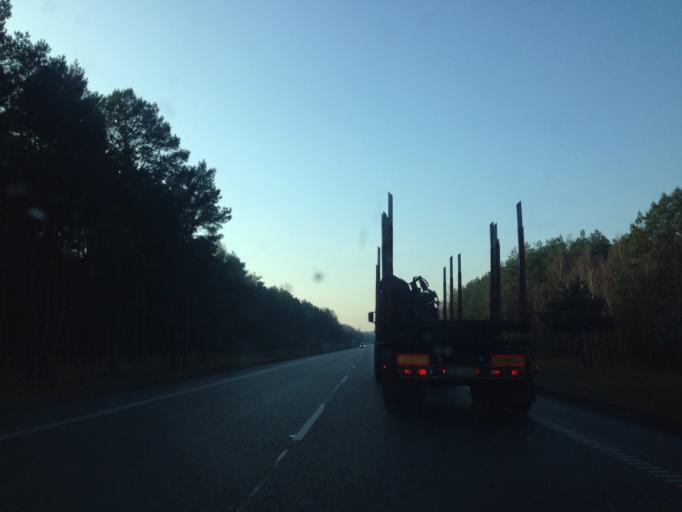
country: PL
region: Kujawsko-Pomorskie
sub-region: Powiat bydgoski
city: Solec Kujawski
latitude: 53.0617
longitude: 18.2049
